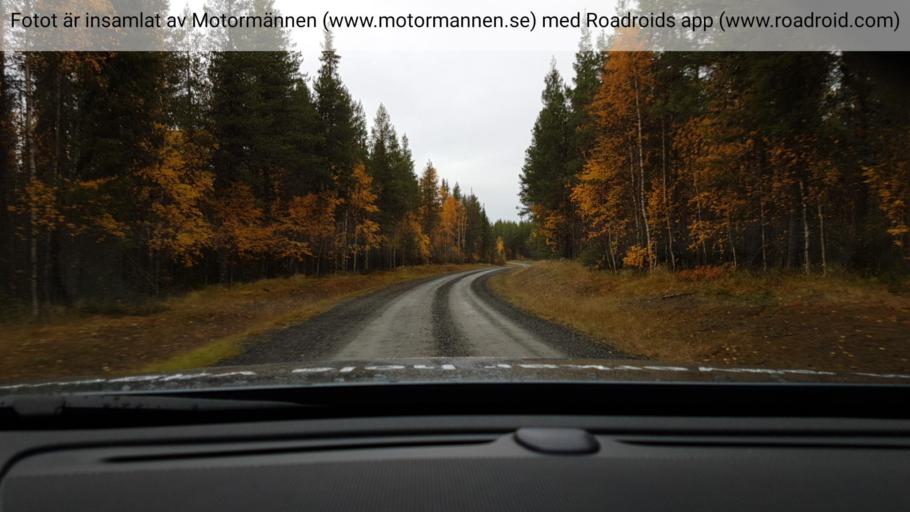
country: SE
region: Norrbotten
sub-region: Pajala Kommun
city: Pajala
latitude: 67.1051
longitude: 22.7032
